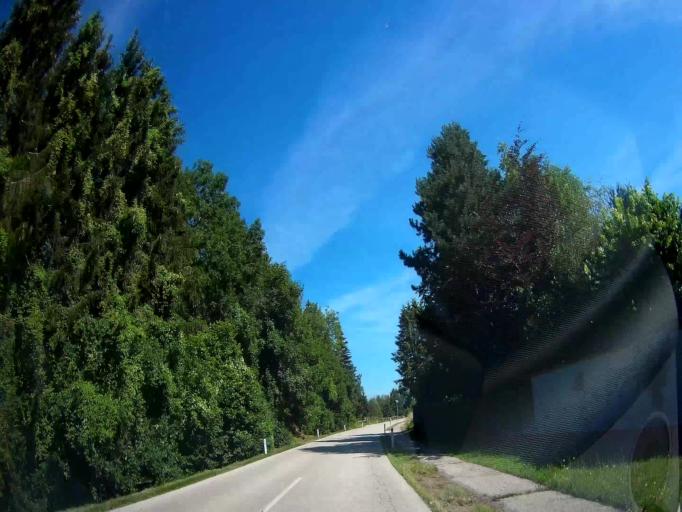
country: AT
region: Carinthia
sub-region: Politischer Bezirk Sankt Veit an der Glan
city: St. Georgen am Laengsee
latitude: 46.7741
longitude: 14.4244
